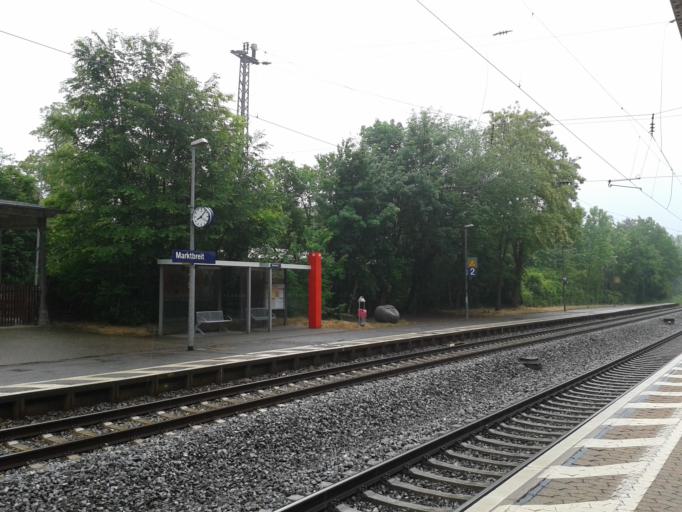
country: DE
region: Bavaria
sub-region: Regierungsbezirk Unterfranken
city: Marktbreit
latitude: 49.6638
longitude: 10.1457
